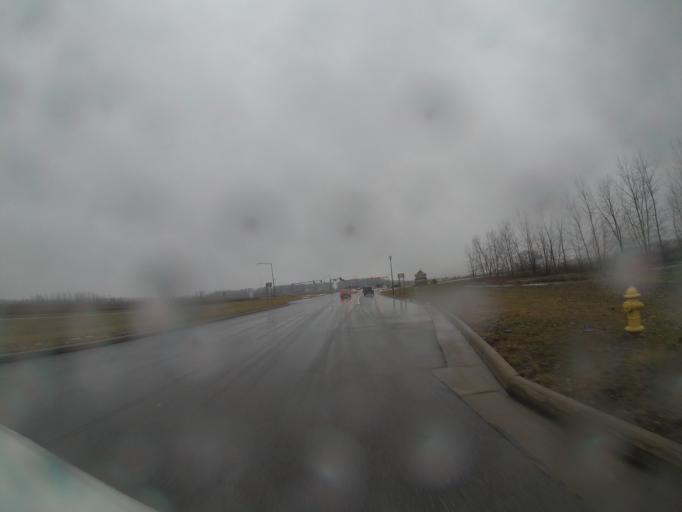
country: US
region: Ohio
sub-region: Wood County
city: Perrysburg
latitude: 41.5600
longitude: -83.5791
